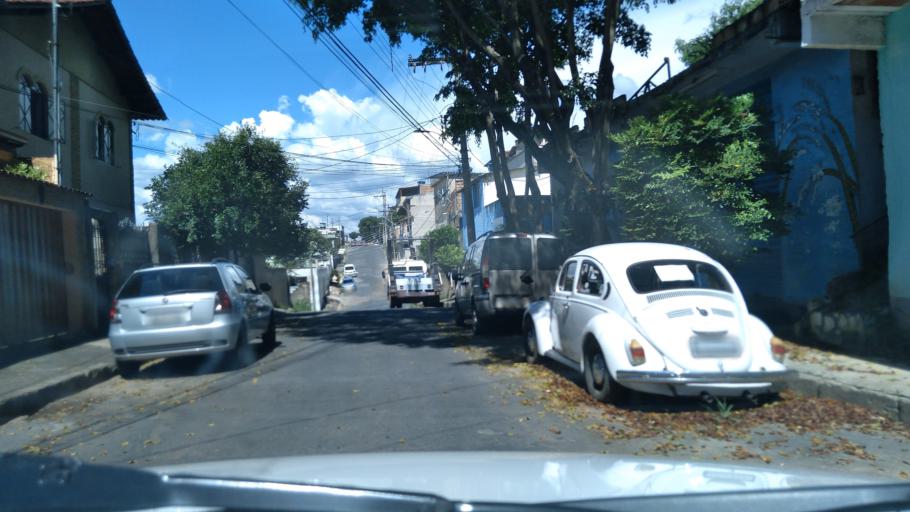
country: BR
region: Minas Gerais
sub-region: Belo Horizonte
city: Belo Horizonte
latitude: -19.8730
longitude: -43.9111
